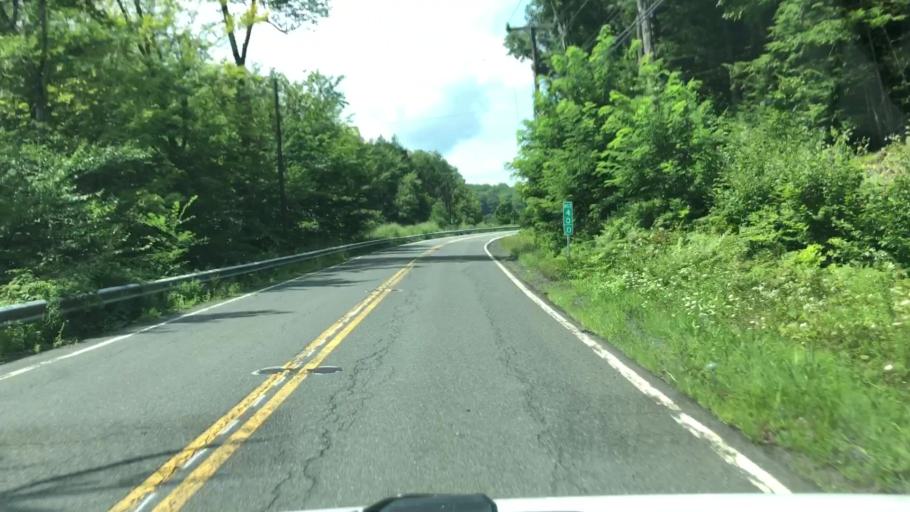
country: US
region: Massachusetts
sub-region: Franklin County
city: Conway
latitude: 42.5127
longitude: -72.7397
